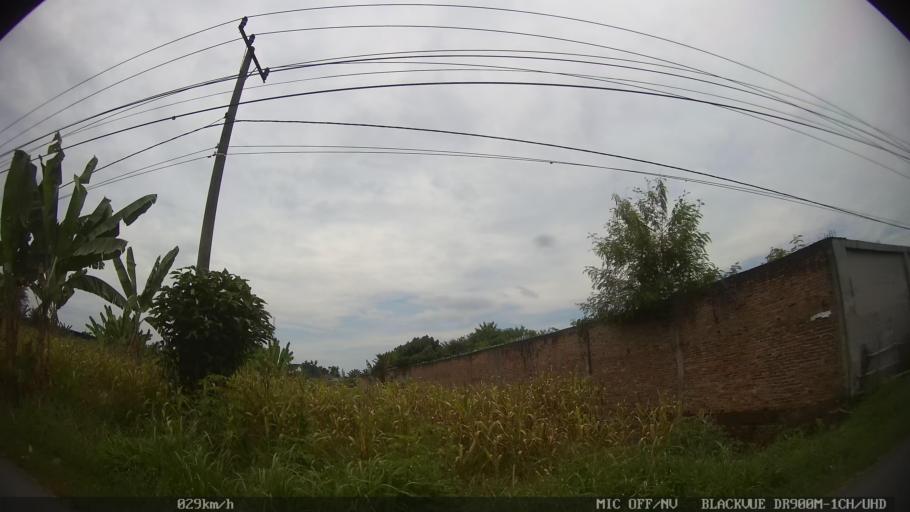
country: ID
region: North Sumatra
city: Binjai
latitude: 3.6212
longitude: 98.5547
